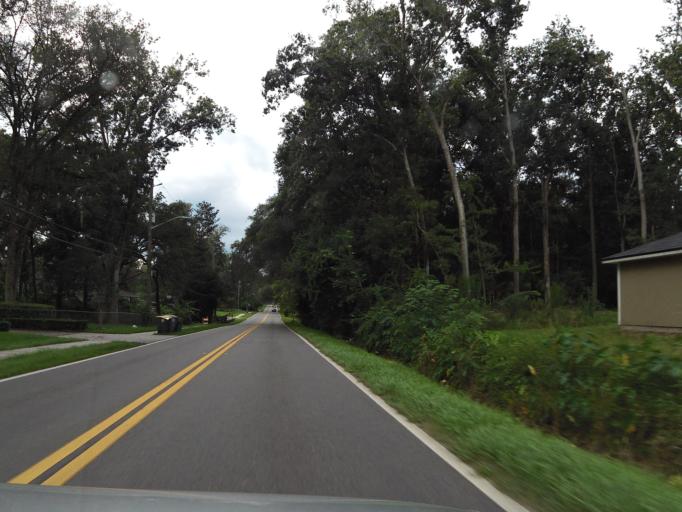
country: US
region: Florida
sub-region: Clay County
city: Bellair-Meadowbrook Terrace
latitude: 30.2848
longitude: -81.7595
